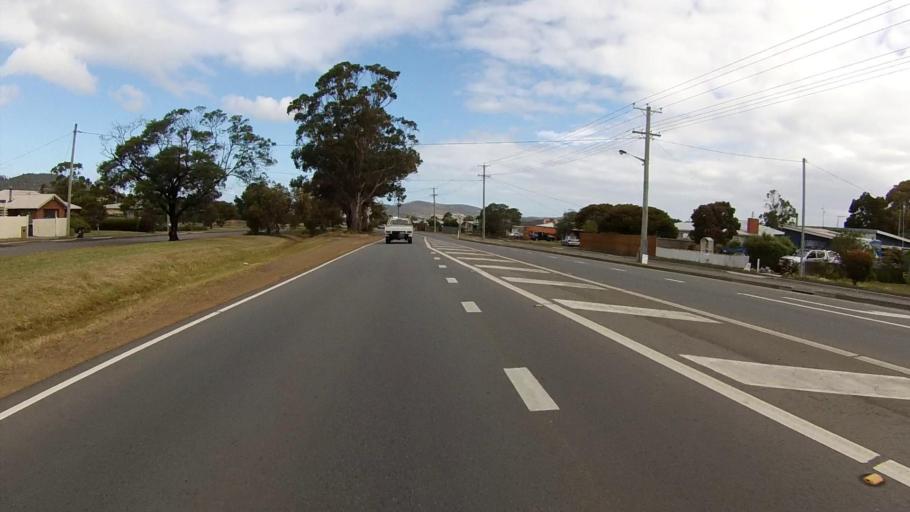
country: AU
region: Tasmania
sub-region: Clarence
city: Rokeby
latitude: -42.8948
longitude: 147.4378
